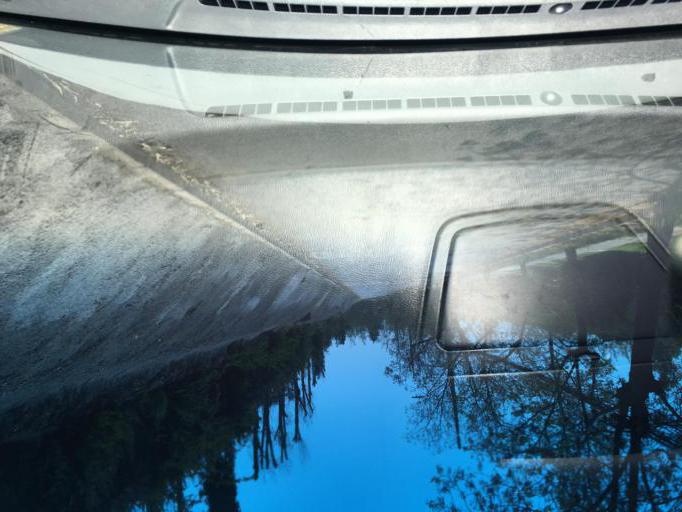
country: CL
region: Santiago Metropolitan
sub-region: Provincia de Santiago
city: Villa Presidente Frei, Nunoa, Santiago, Chile
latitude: -33.5266
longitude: -70.5691
